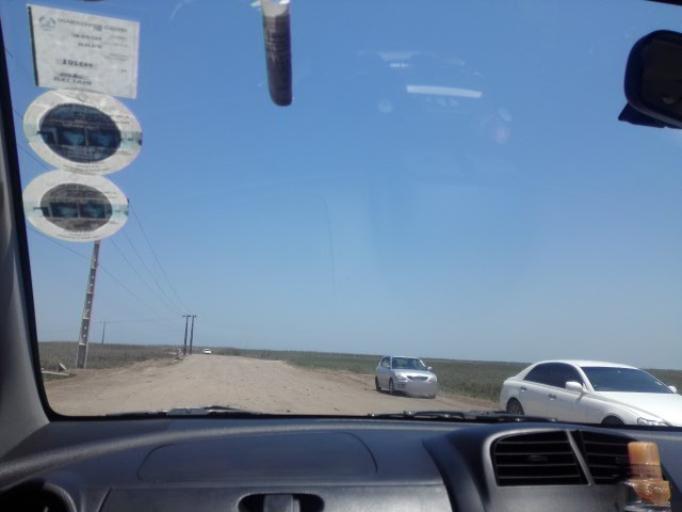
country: MZ
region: Maputo City
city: Maputo
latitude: -25.7333
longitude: 32.7214
